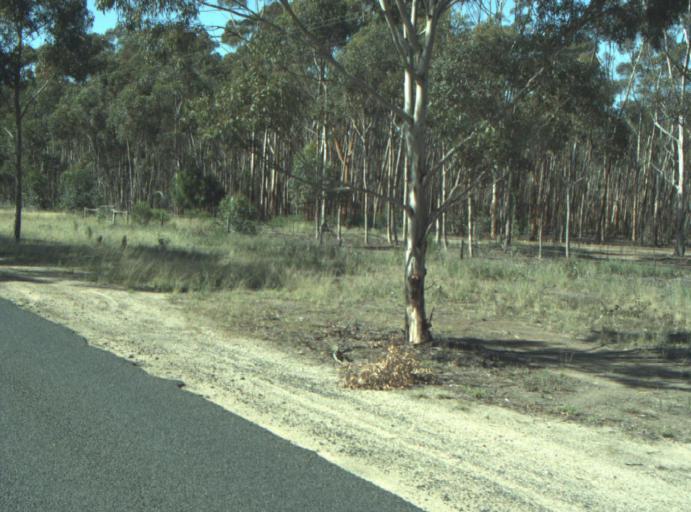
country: AU
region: Victoria
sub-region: Greater Geelong
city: Lara
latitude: -37.9494
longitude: 144.3938
